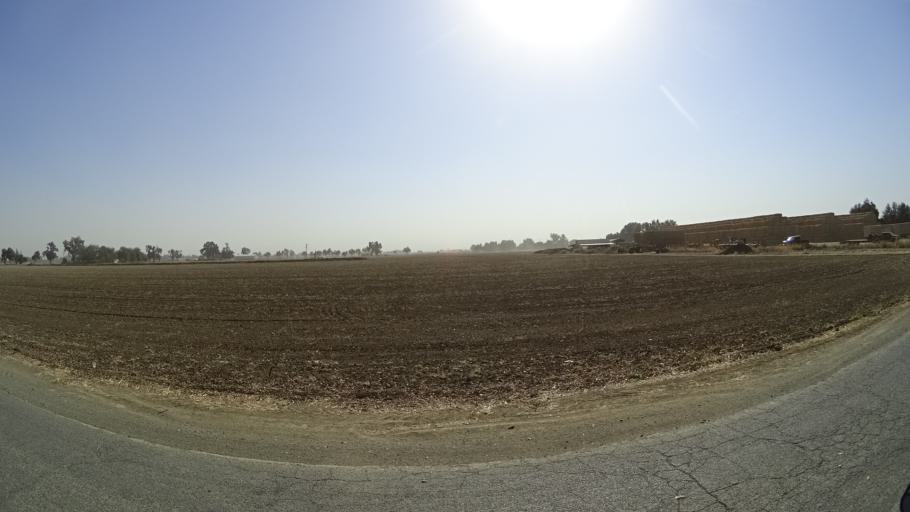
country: US
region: California
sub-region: Yolo County
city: Woodland
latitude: 38.7422
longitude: -121.7800
